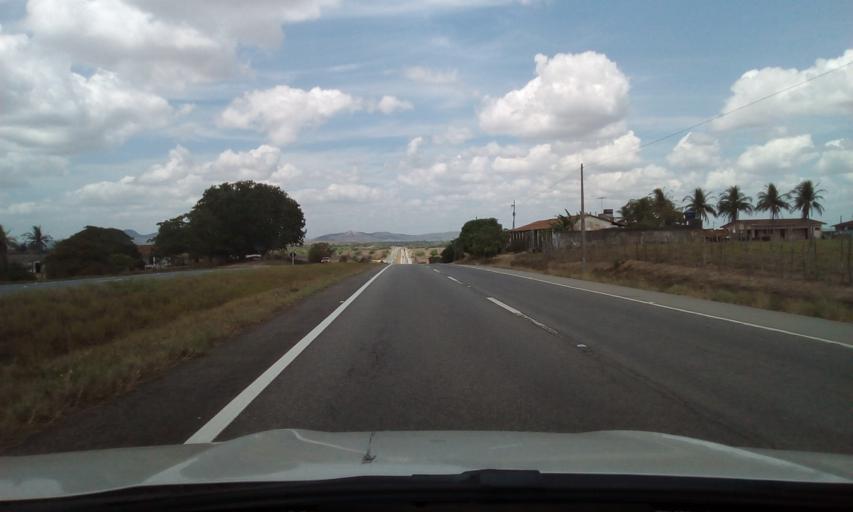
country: BR
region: Paraiba
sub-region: Pilar
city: Pilar
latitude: -7.1818
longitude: -35.3083
